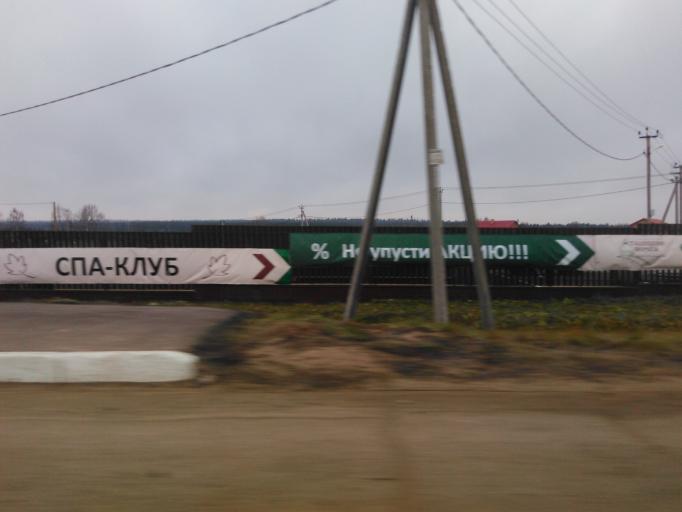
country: RU
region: Moskovskaya
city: Ashukino
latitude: 56.1710
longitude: 37.9399
